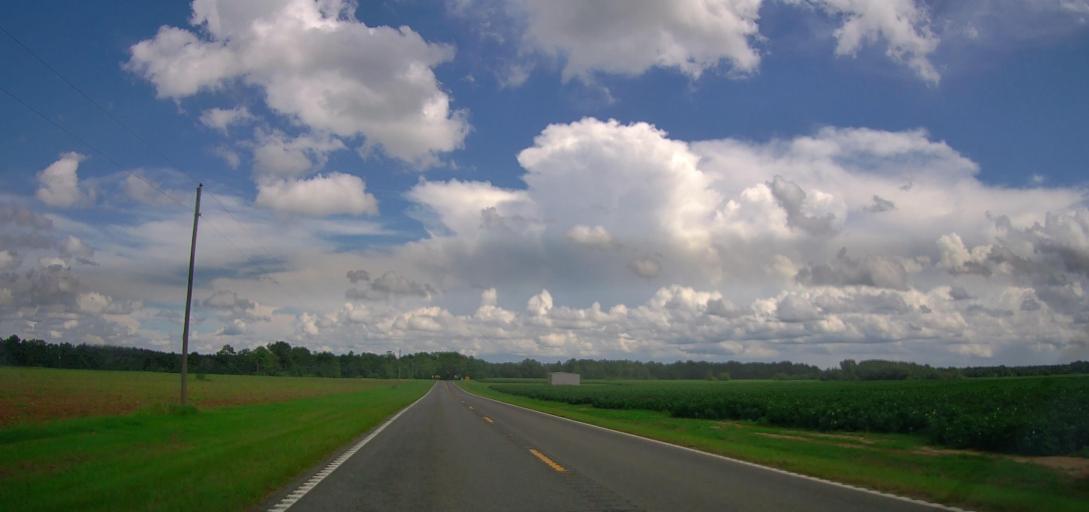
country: US
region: Georgia
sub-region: Taylor County
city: Reynolds
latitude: 32.4400
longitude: -84.0814
